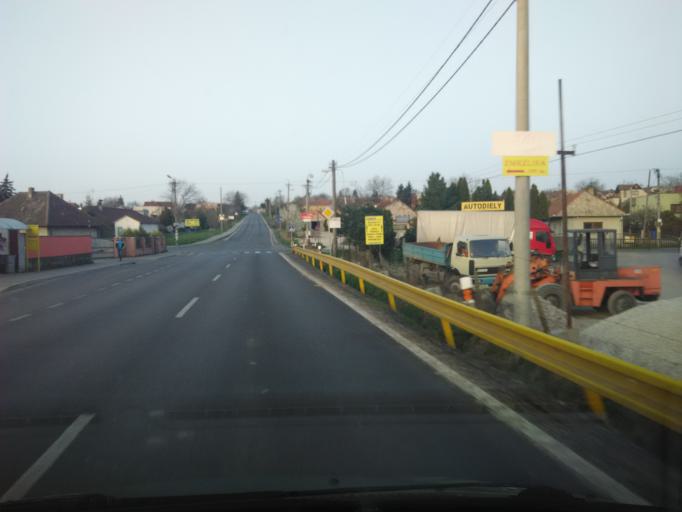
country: SK
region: Nitriansky
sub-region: Okres Nitra
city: Nitra
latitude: 48.2463
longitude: 18.0216
